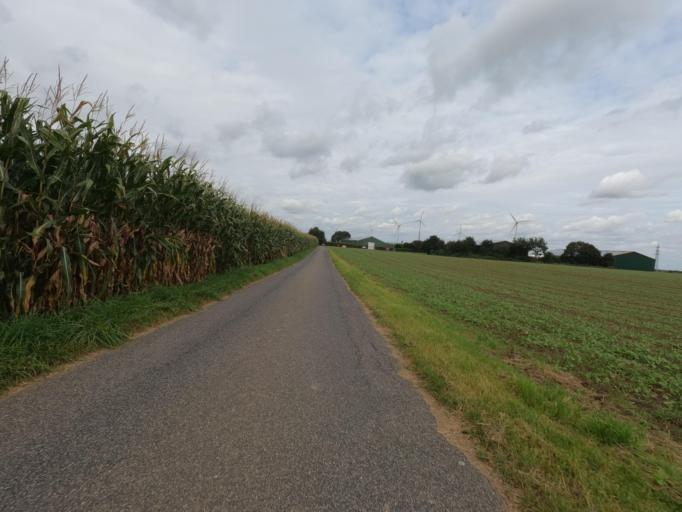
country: DE
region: North Rhine-Westphalia
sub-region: Regierungsbezirk Koln
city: Ubach-Palenberg
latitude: 50.9213
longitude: 6.1476
